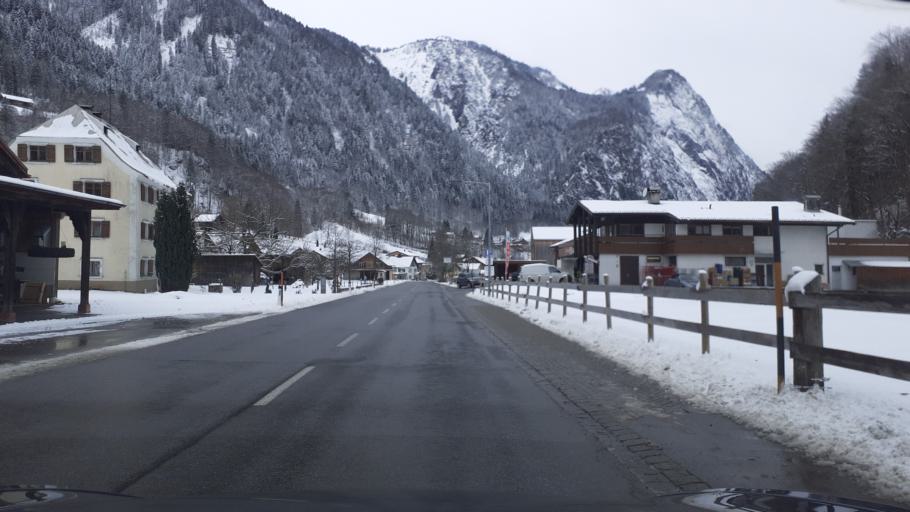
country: AT
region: Vorarlberg
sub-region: Politischer Bezirk Bludenz
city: Dalaas
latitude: 47.1225
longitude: 9.9970
